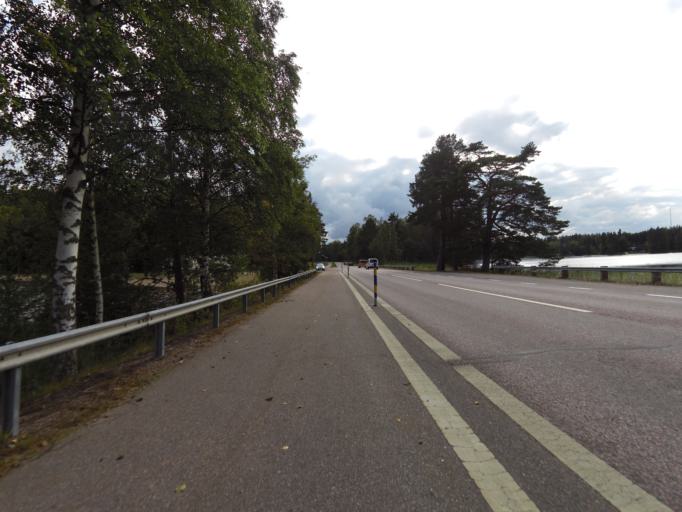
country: SE
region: Gaevleborg
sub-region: Sandvikens Kommun
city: Sandviken
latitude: 60.6925
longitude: 16.8166
